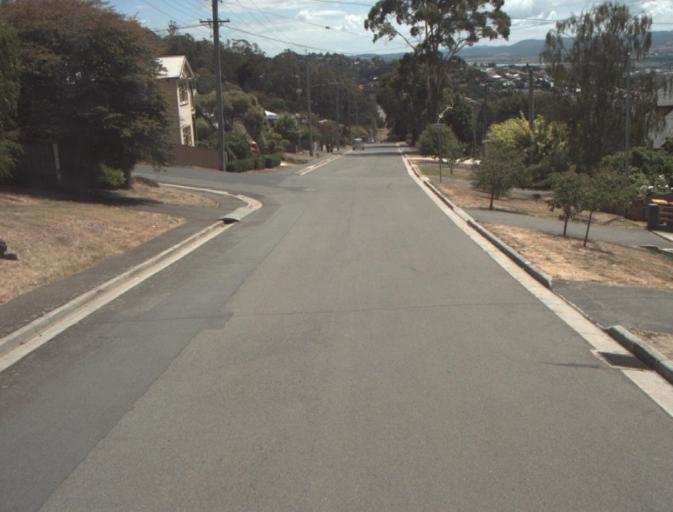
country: AU
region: Tasmania
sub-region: Launceston
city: West Launceston
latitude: -41.4590
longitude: 147.1354
